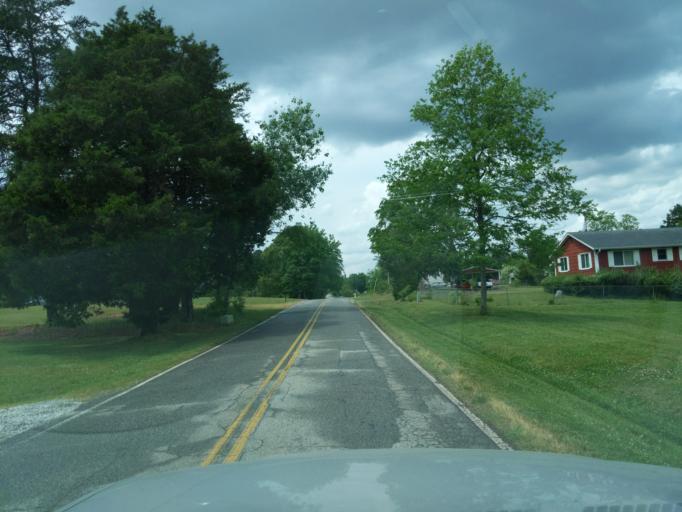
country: US
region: South Carolina
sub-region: Spartanburg County
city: Inman Mills
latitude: 35.0107
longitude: -82.1195
